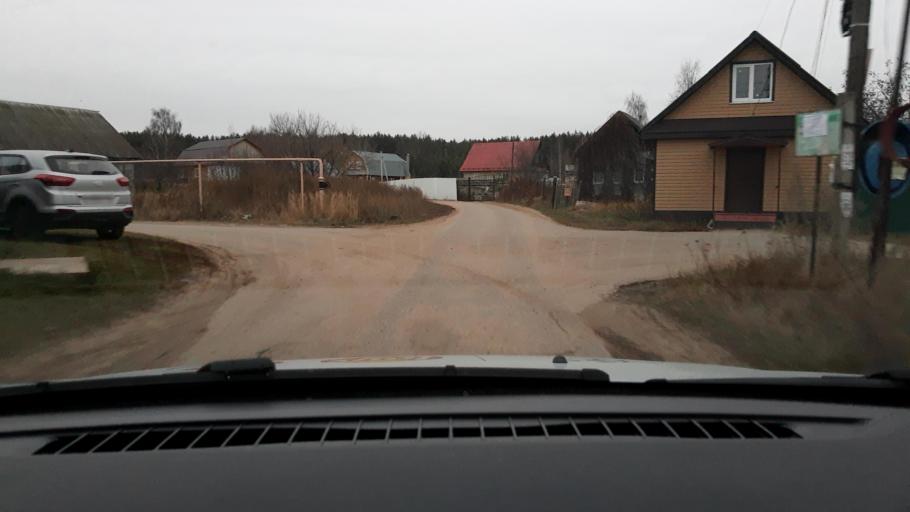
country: RU
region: Nizjnij Novgorod
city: Neklyudovo
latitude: 56.4200
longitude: 44.0211
